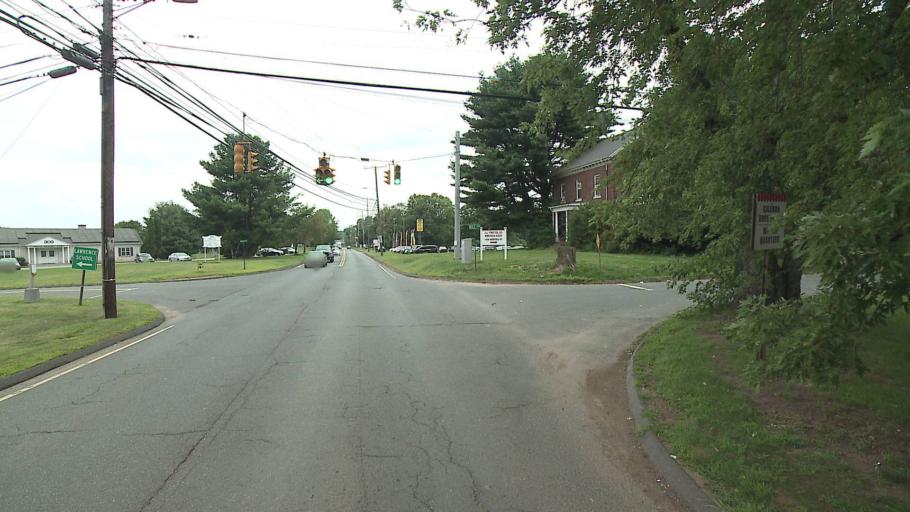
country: US
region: Connecticut
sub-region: Middlesex County
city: Cromwell
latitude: 41.5832
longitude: -72.6732
